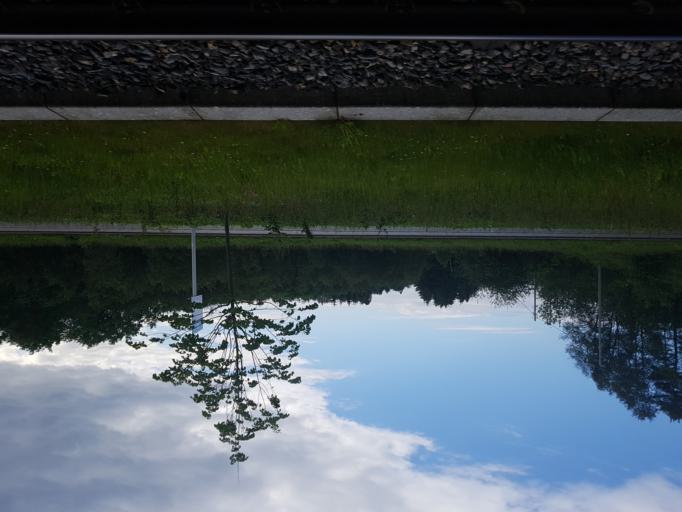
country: NO
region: Hordaland
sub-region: Bergen
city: Ytrebygda
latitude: 60.2922
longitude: 5.2425
